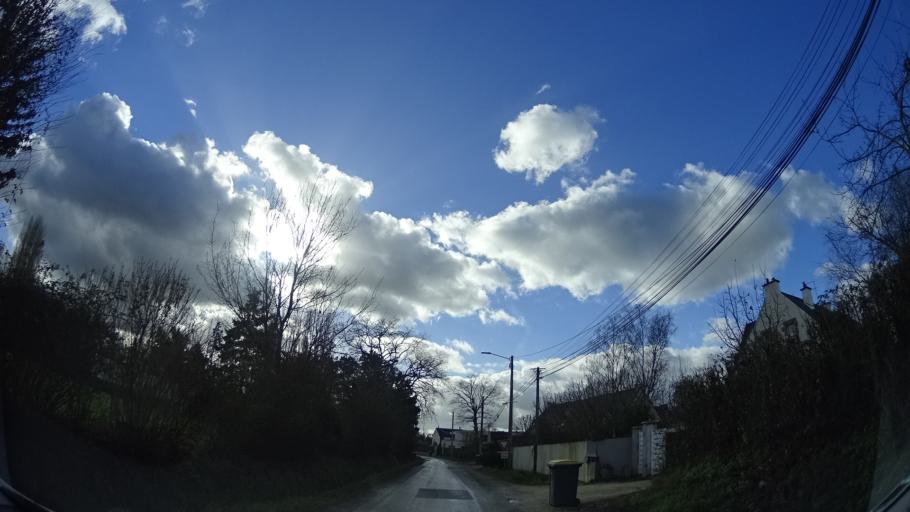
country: FR
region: Brittany
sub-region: Departement d'Ille-et-Vilaine
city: Chantepie
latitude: 48.0777
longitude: -1.6364
